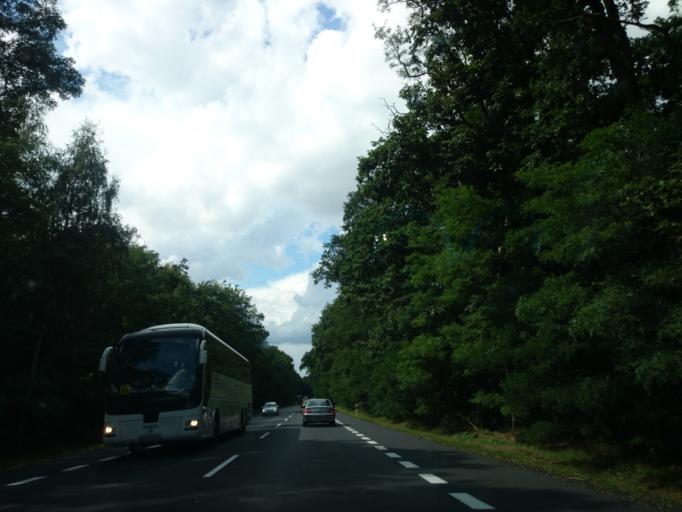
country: PL
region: Lubusz
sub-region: Powiat nowosolski
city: Nowe Miasteczko
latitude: 51.6815
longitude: 15.7653
